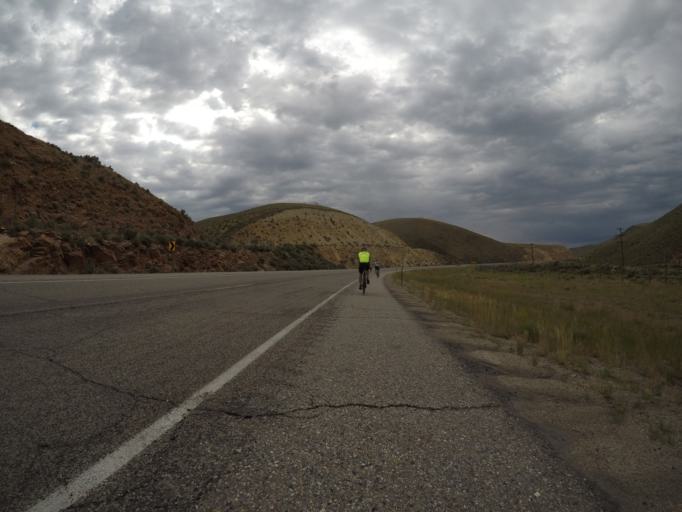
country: US
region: Wyoming
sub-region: Lincoln County
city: Kemmerer
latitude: 41.8257
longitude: -110.8107
